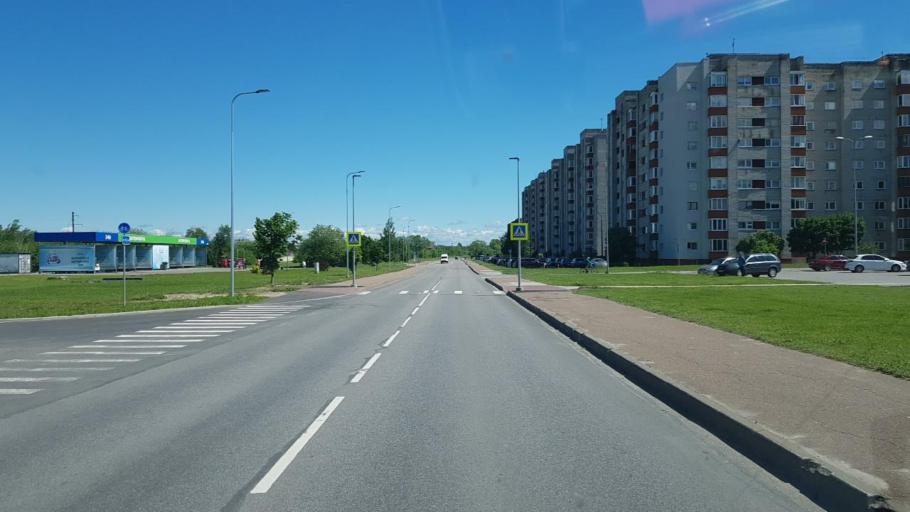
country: EE
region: Ida-Virumaa
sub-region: Narva linn
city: Narva
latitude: 59.3875
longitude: 28.1781
